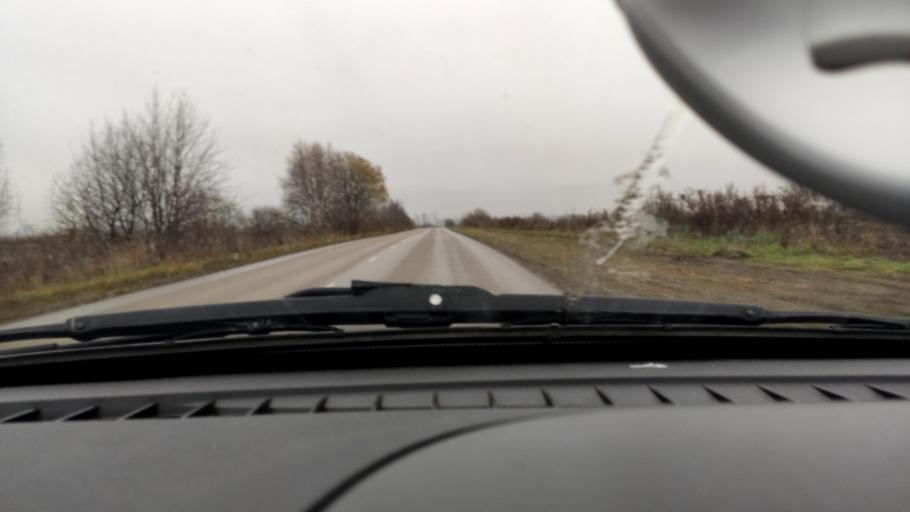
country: RU
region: Perm
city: Kondratovo
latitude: 57.9992
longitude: 56.0757
